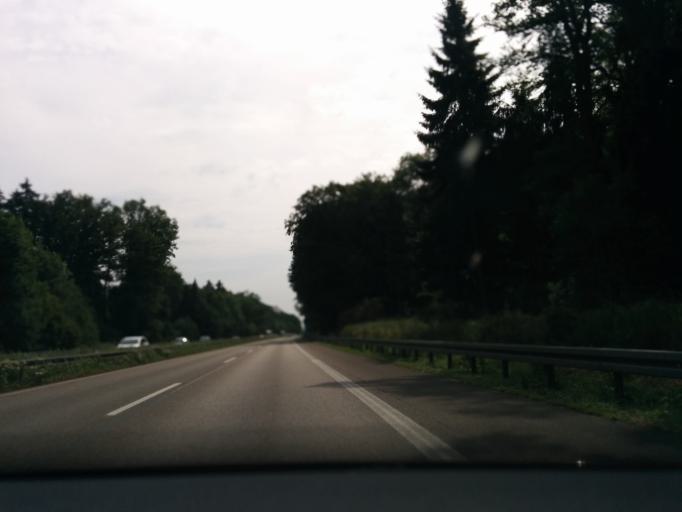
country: DE
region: Baden-Wuerttemberg
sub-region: Tuebingen Region
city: Beimerstetten
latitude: 48.4577
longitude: 10.0097
